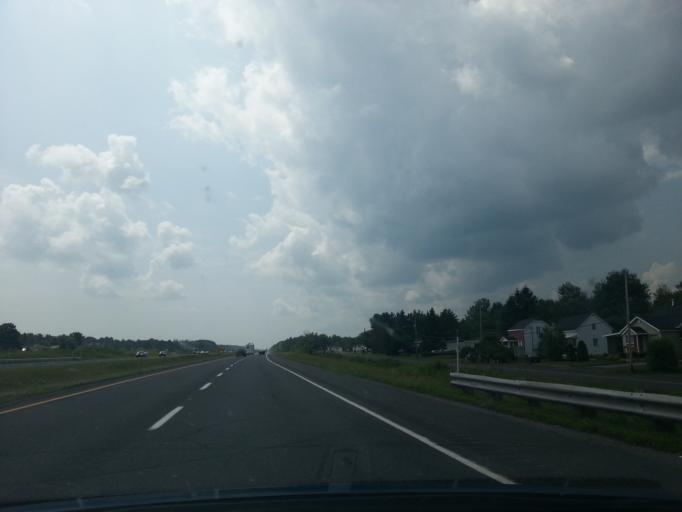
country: CA
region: Quebec
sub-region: Chaudiere-Appalaches
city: Saint-Antoine-de-Tilly
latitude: 46.6128
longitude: -71.5178
